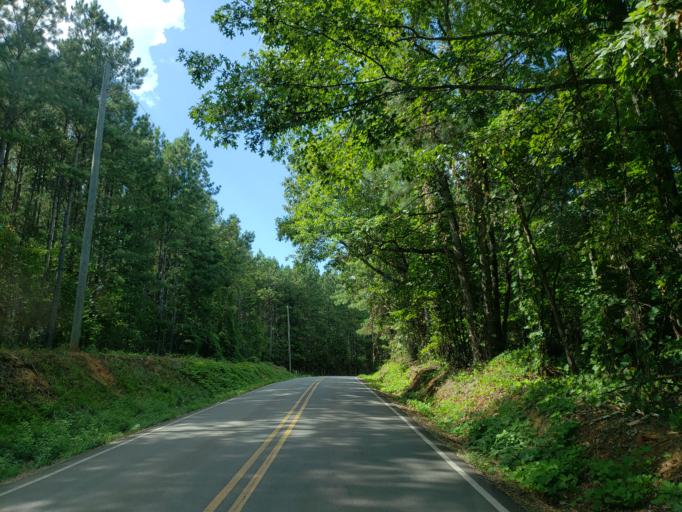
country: US
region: Georgia
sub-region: Pickens County
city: Jasper
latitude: 34.4258
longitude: -84.4400
